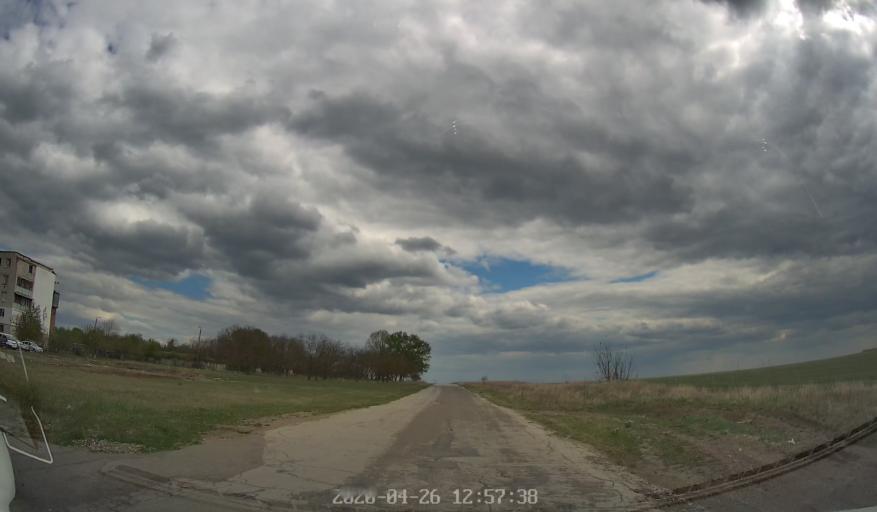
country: MD
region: Chisinau
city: Vadul lui Voda
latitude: 47.0681
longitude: 29.0775
